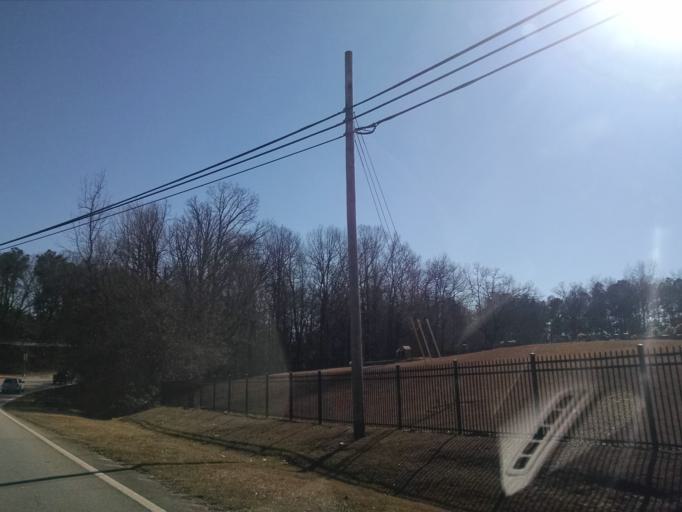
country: US
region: Georgia
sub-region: Gwinnett County
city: Suwanee
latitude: 34.0837
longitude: -84.0728
